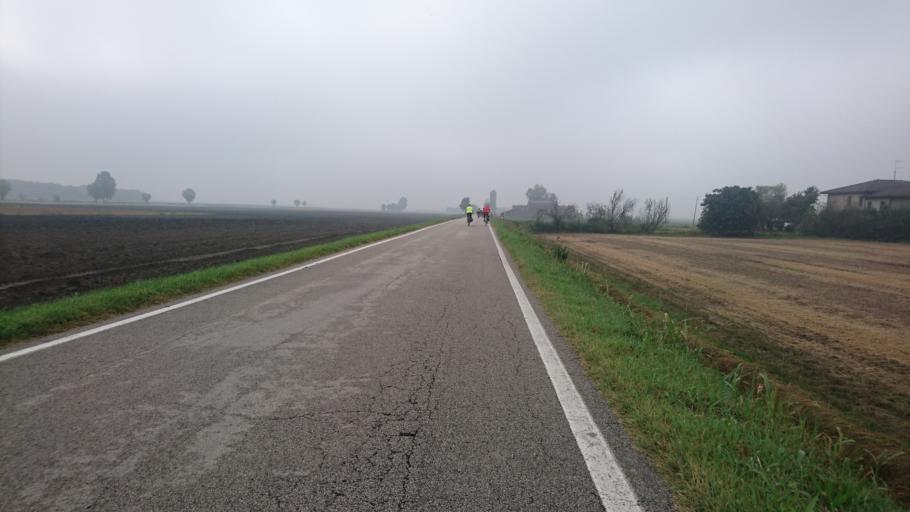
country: IT
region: Veneto
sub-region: Provincia di Padova
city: Pozzonovo
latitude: 45.1775
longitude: 11.7874
